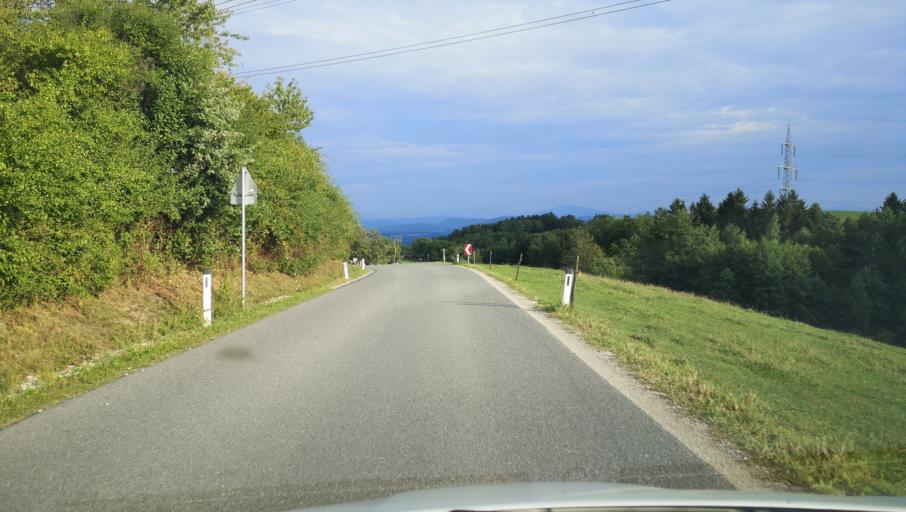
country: AT
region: Lower Austria
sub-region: Politischer Bezirk Amstetten
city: Sankt Georgen am Ybbsfelde
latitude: 48.1506
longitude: 14.9521
